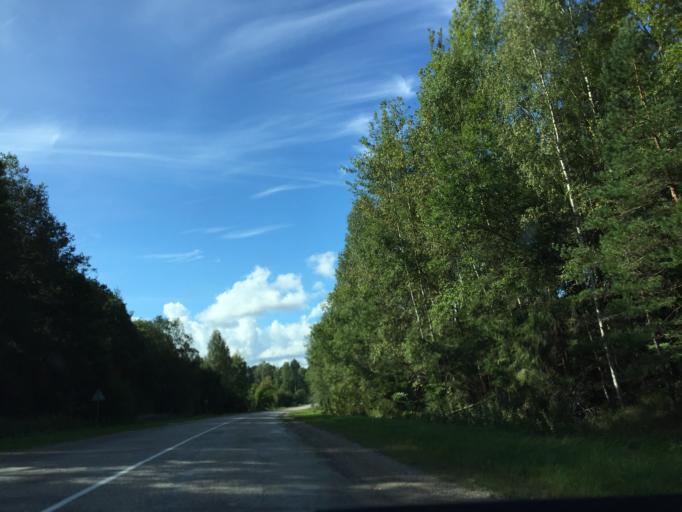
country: LV
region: Kuldigas Rajons
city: Kuldiga
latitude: 56.9890
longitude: 21.7772
